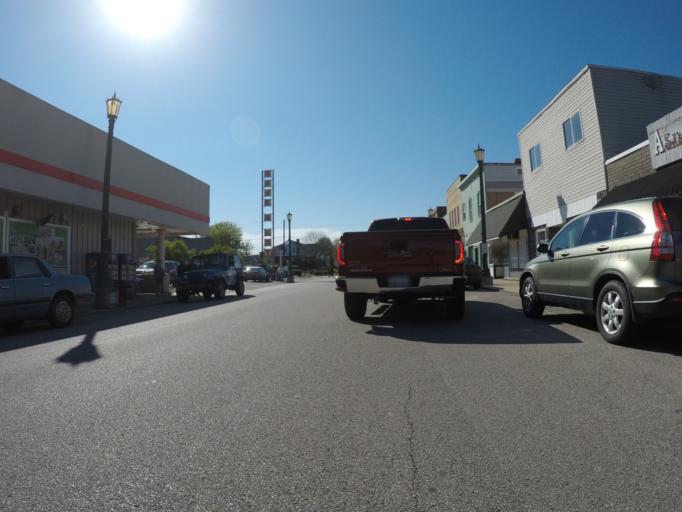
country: US
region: West Virginia
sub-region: Wayne County
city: Kenova
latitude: 38.3994
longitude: -82.5784
